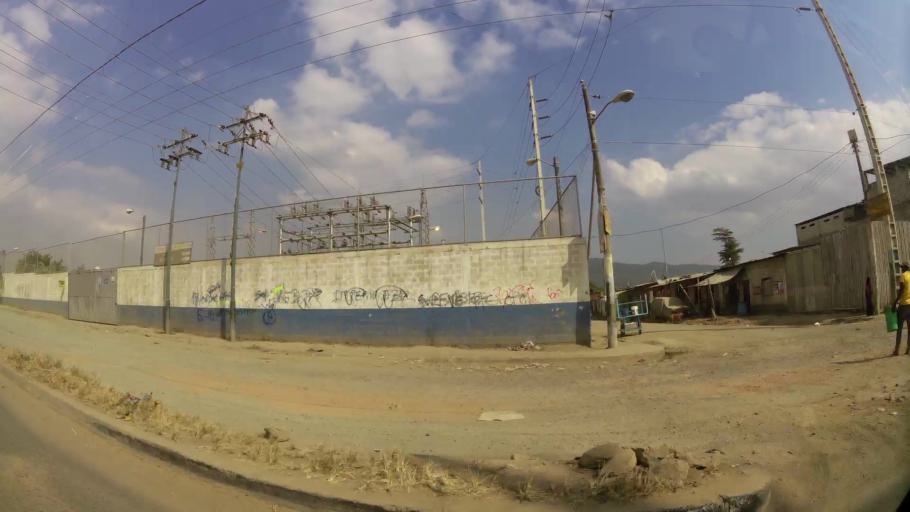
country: EC
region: Guayas
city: Santa Lucia
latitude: -2.1209
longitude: -79.9857
